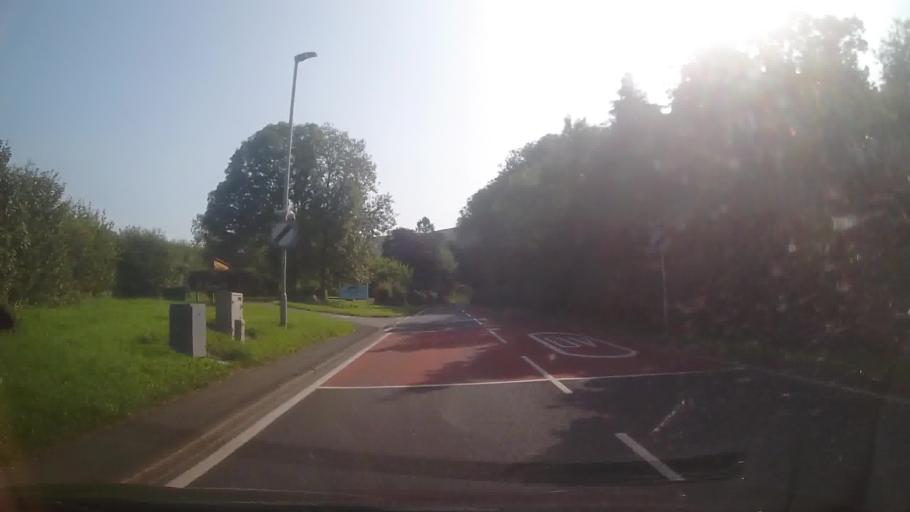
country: GB
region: Wales
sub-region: Sir Powys
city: Rhayader
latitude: 52.2977
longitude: -3.5030
